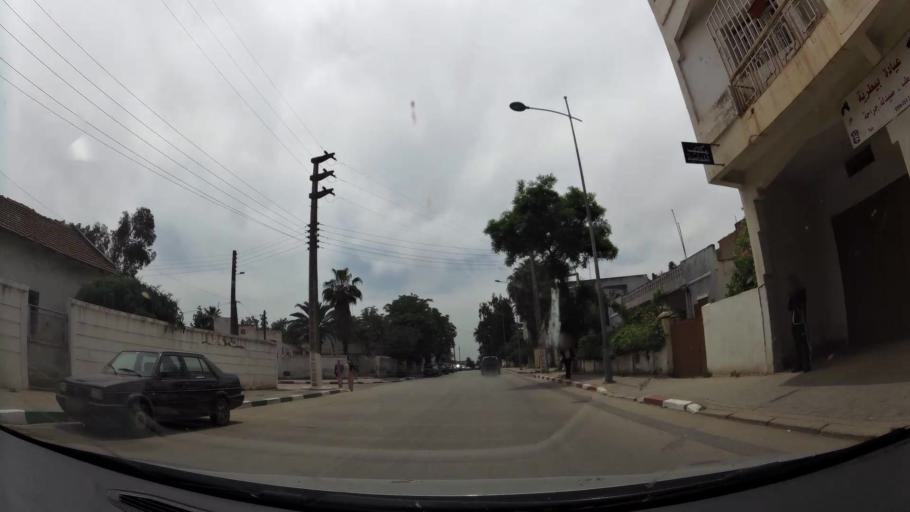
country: MA
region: Rabat-Sale-Zemmour-Zaer
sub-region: Khemisset
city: Khemisset
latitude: 33.8222
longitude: -6.0661
